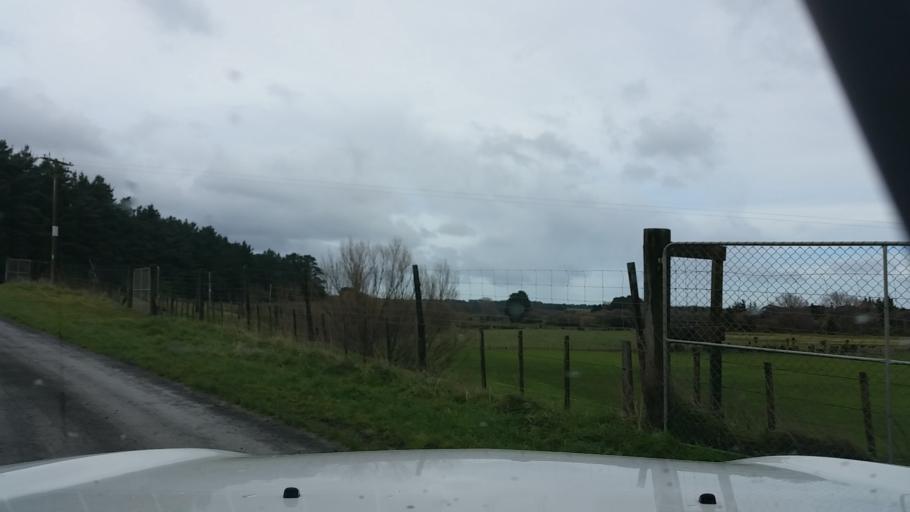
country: NZ
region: Wellington
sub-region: Upper Hutt City
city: Upper Hutt
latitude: -41.3451
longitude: 175.2184
